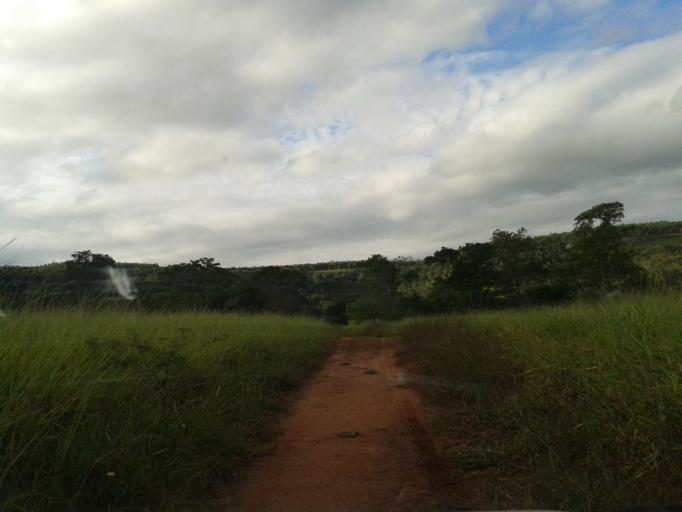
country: BR
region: Minas Gerais
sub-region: Campina Verde
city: Campina Verde
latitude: -19.4600
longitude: -49.6315
